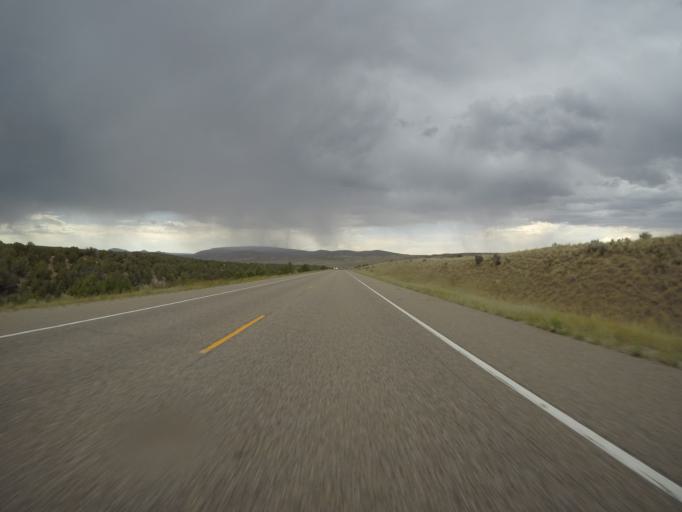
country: US
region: Colorado
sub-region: Rio Blanco County
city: Rangely
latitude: 40.3935
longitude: -108.3462
